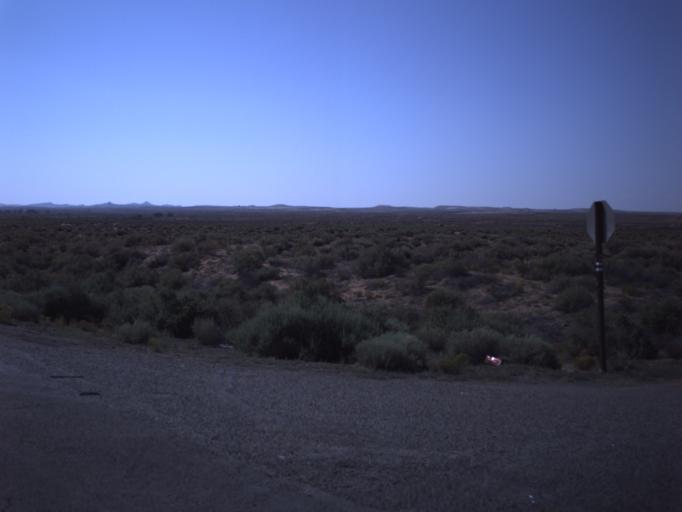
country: US
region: Utah
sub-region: San Juan County
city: Blanding
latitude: 37.1815
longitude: -109.5887
